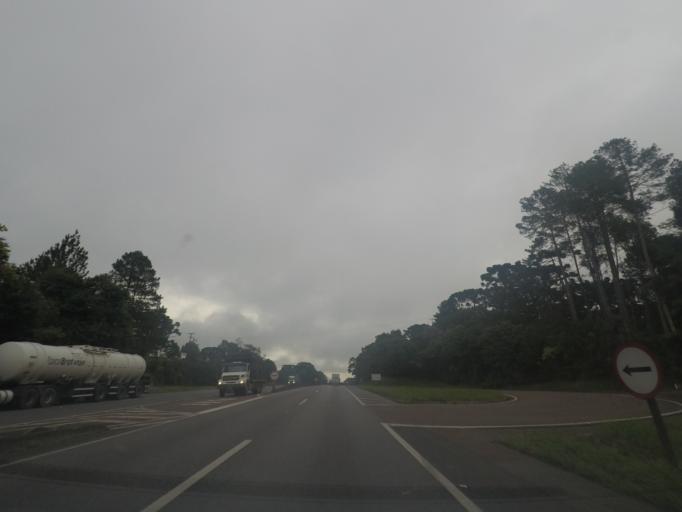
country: BR
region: Parana
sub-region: Campina Grande Do Sul
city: Campina Grande do Sul
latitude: -25.3070
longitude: -48.9778
